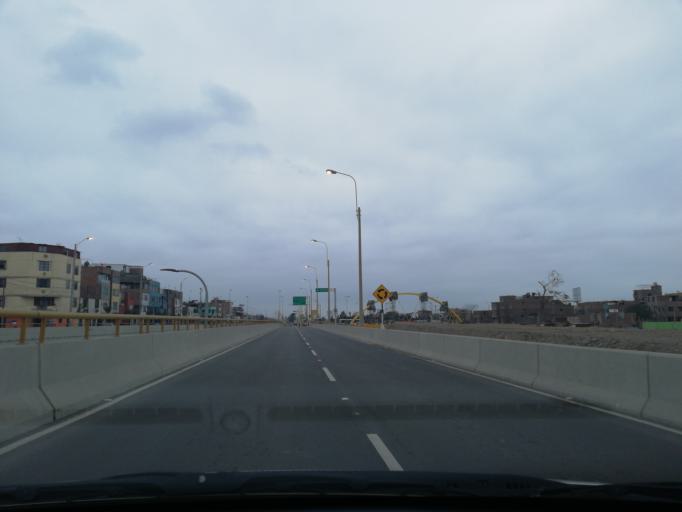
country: PE
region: Callao
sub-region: Callao
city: Callao
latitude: -12.0353
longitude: -77.0757
